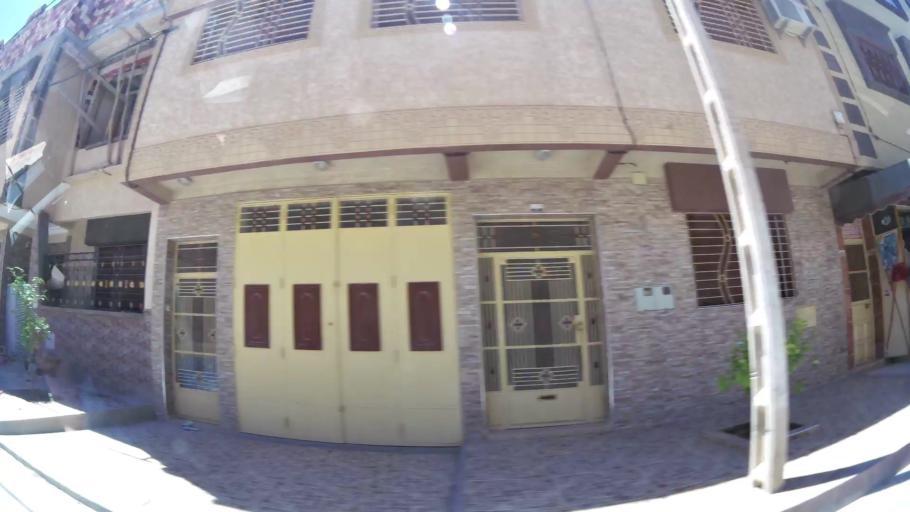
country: MA
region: Oriental
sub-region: Oujda-Angad
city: Oujda
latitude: 34.6777
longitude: -1.8624
